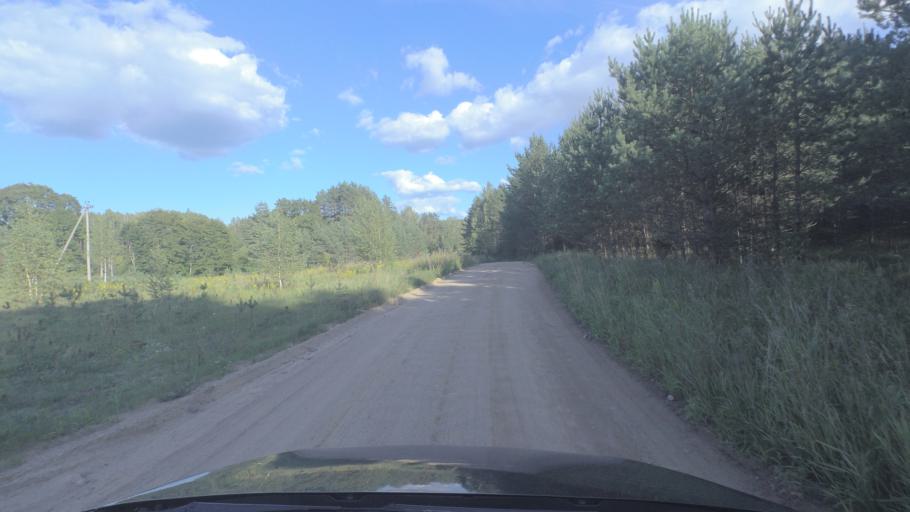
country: LT
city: Pabrade
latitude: 55.1401
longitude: 25.7213
